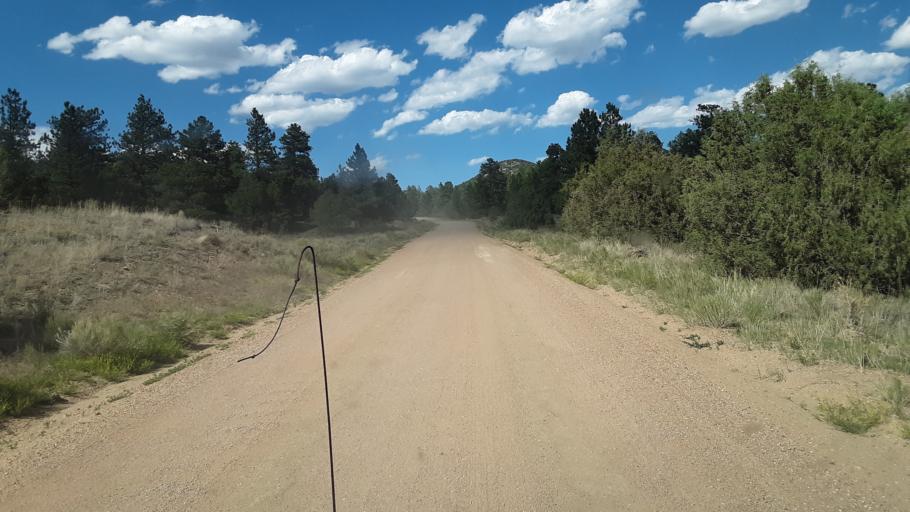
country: US
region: Colorado
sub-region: Custer County
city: Westcliffe
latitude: 38.2520
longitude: -105.5508
